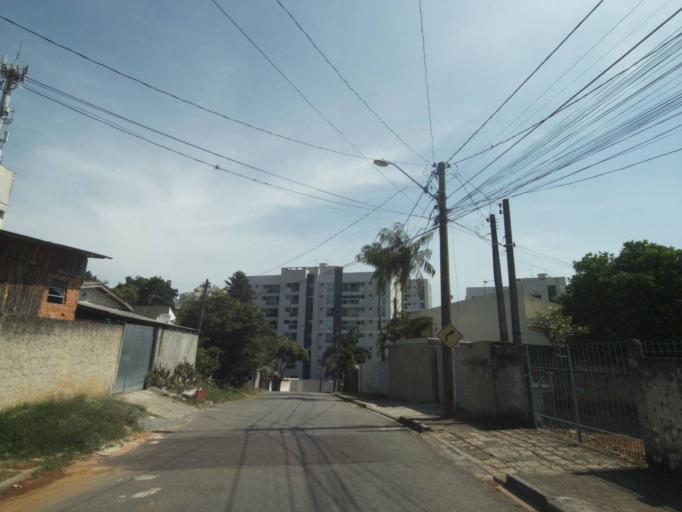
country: BR
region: Parana
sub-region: Curitiba
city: Curitiba
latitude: -25.4705
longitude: -49.2983
